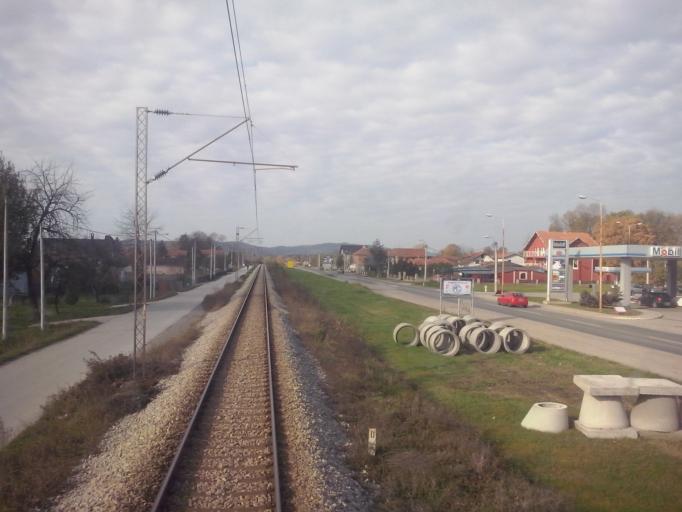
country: RS
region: Central Serbia
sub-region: Kolubarski Okrug
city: Lajkovac
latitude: 44.3647
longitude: 20.1475
